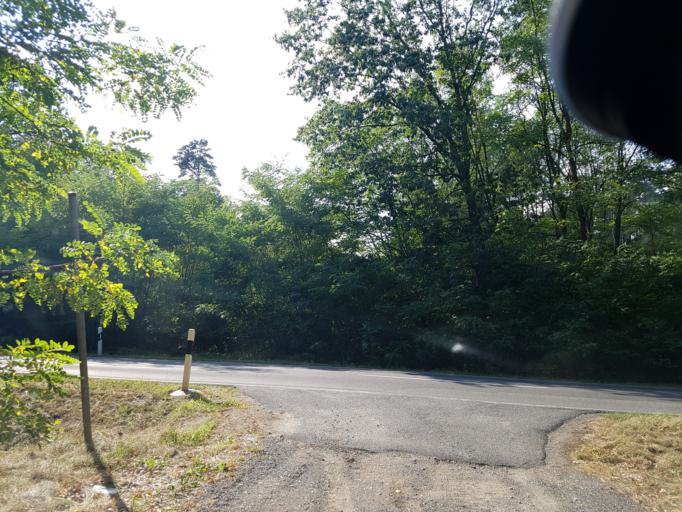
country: DE
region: Brandenburg
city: Calau
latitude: 51.7725
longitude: 13.9523
